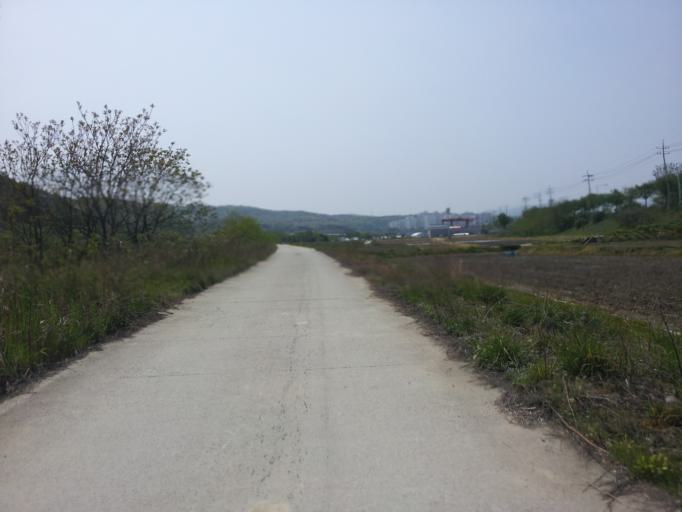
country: KR
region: Daejeon
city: Daejeon
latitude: 36.2661
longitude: 127.2884
